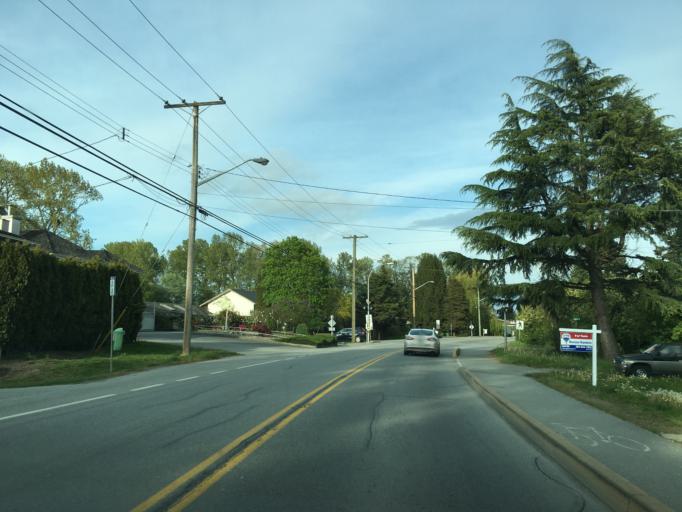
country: CA
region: British Columbia
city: New Westminster
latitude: 49.1814
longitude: -122.9651
